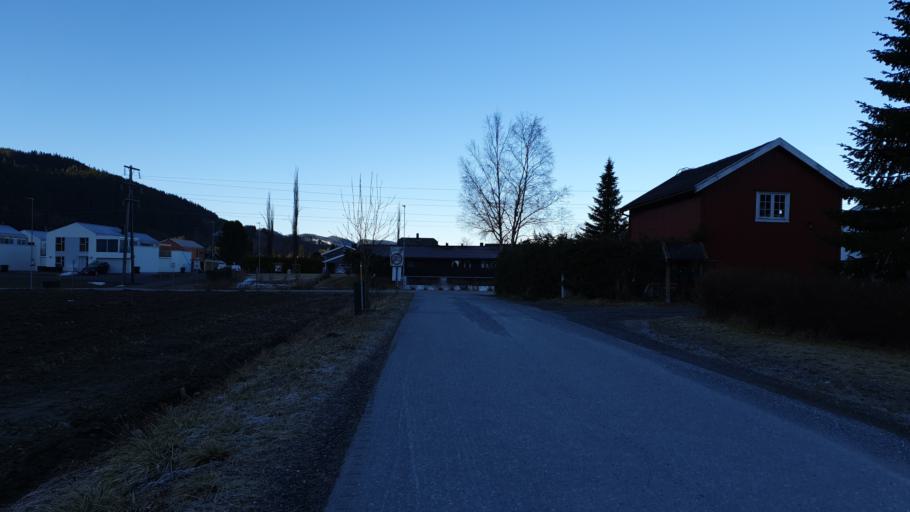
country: NO
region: Sor-Trondelag
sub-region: Orkdal
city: Orkanger
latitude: 63.2902
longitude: 9.8472
